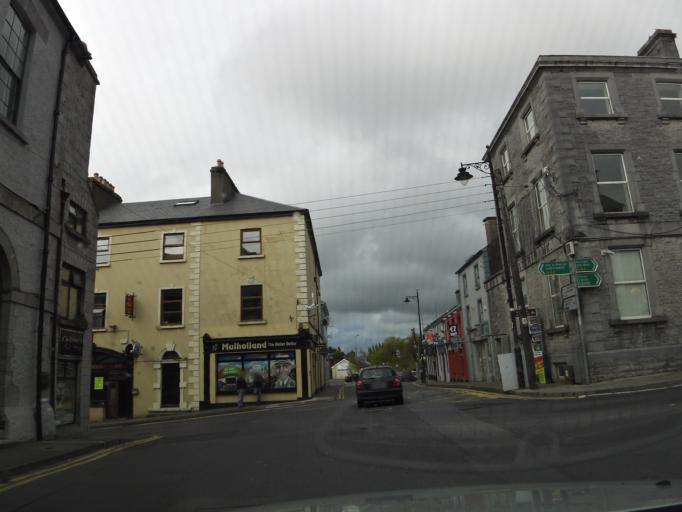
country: IE
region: Connaught
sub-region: Maigh Eo
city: Ballinrobe
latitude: 53.6239
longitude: -9.2224
